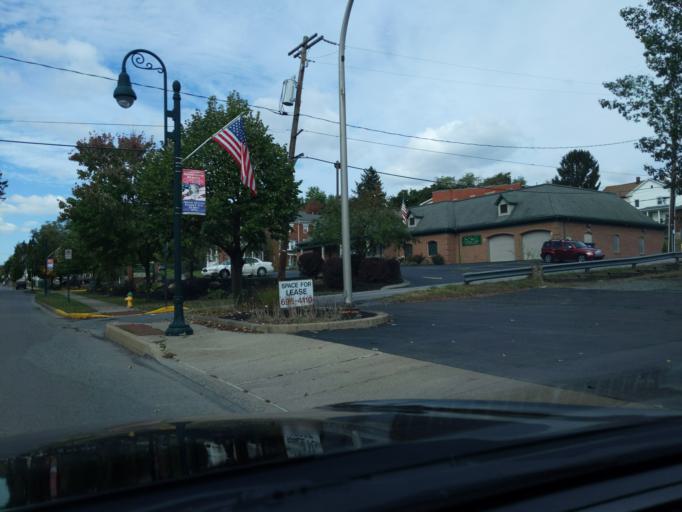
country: US
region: Pennsylvania
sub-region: Blair County
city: Hollidaysburg
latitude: 40.4284
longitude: -78.3971
